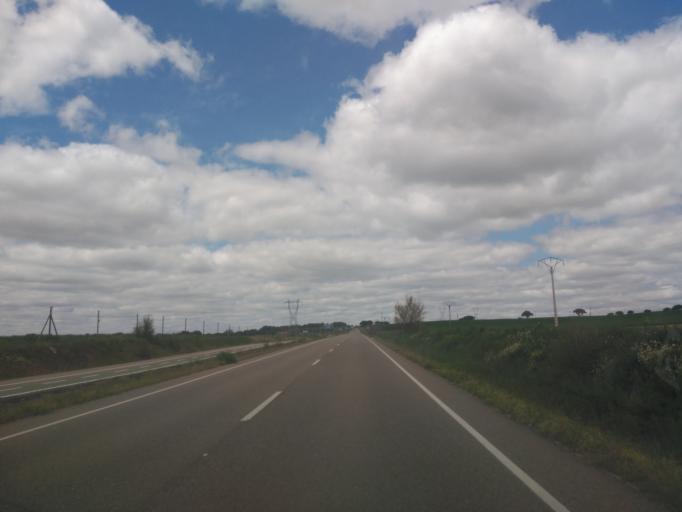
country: ES
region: Castille and Leon
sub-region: Provincia de Salamanca
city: Florida de Liebana
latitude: 41.0273
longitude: -5.7262
